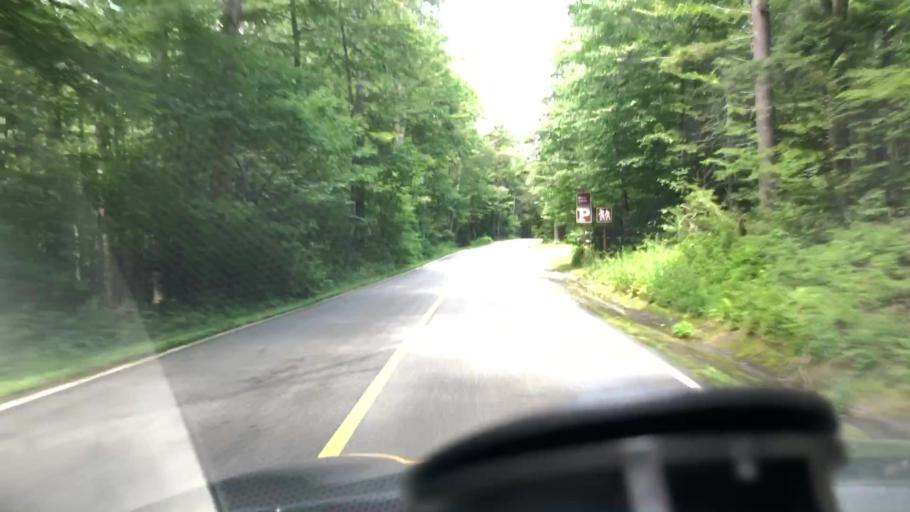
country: US
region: Massachusetts
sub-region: Berkshire County
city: Williamstown
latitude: 42.6685
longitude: -73.1671
